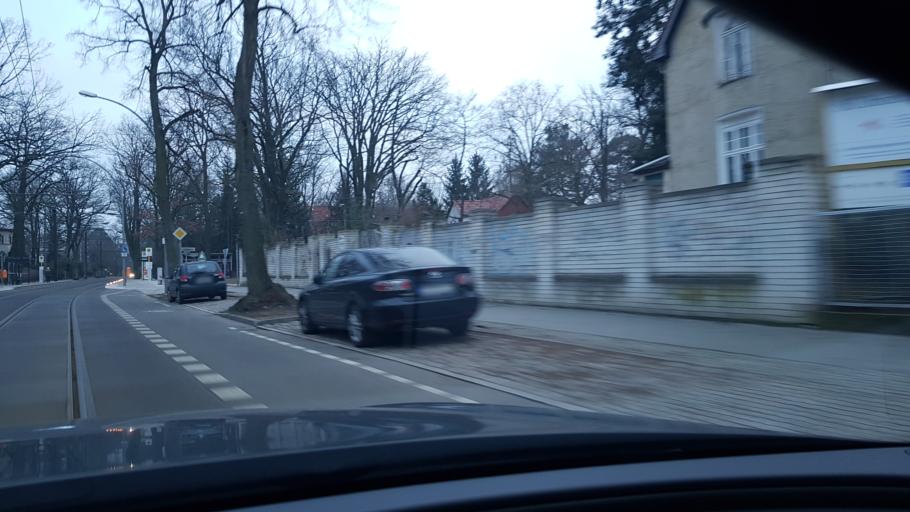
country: DE
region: Berlin
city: Grunau
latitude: 52.4227
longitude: 13.5875
